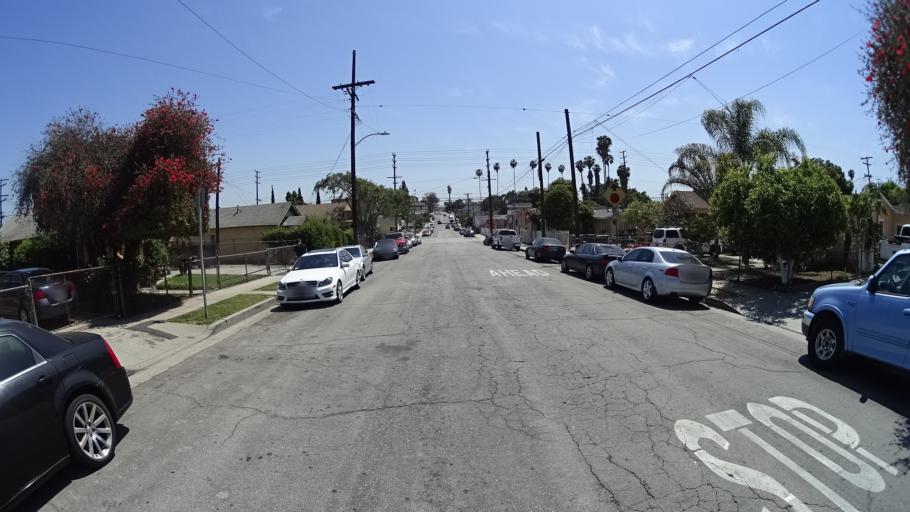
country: US
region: California
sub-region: Los Angeles County
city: Belvedere
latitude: 34.0430
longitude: -118.1823
